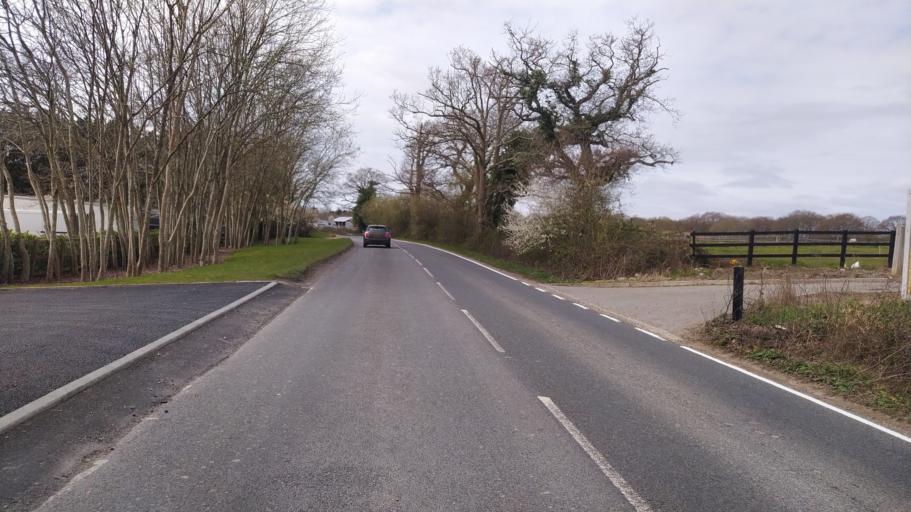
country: GB
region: England
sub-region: Hampshire
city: Wickham
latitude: 50.8748
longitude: -1.2216
